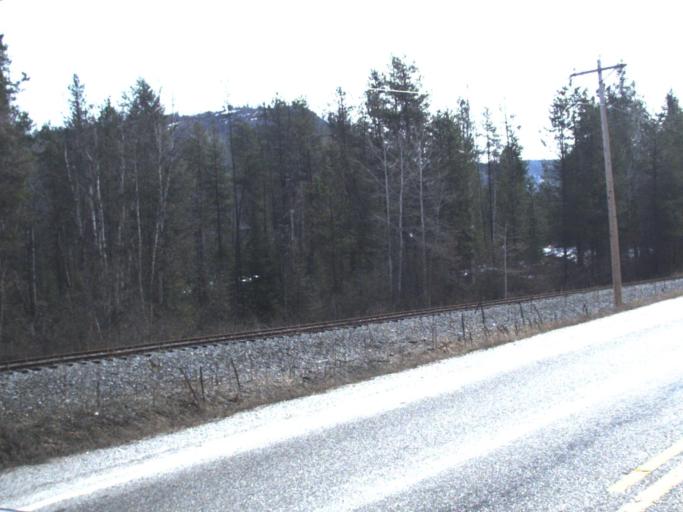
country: CA
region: British Columbia
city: Fruitvale
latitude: 48.6502
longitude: -117.3813
